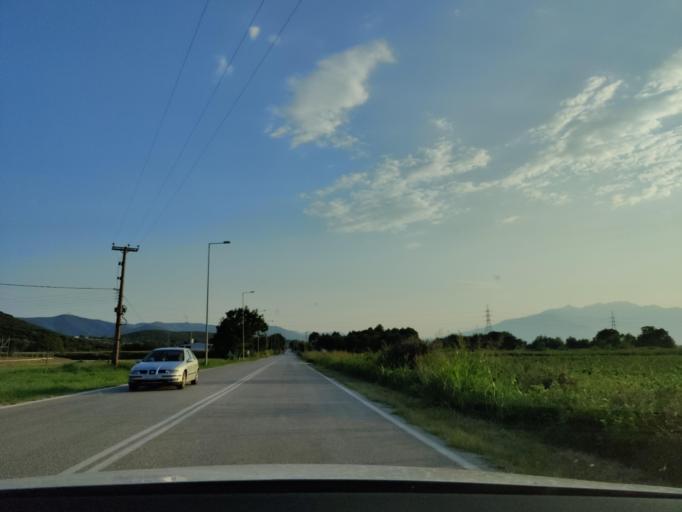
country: GR
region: East Macedonia and Thrace
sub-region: Nomos Kavalas
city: Amygdaleonas
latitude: 40.9857
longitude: 24.3723
